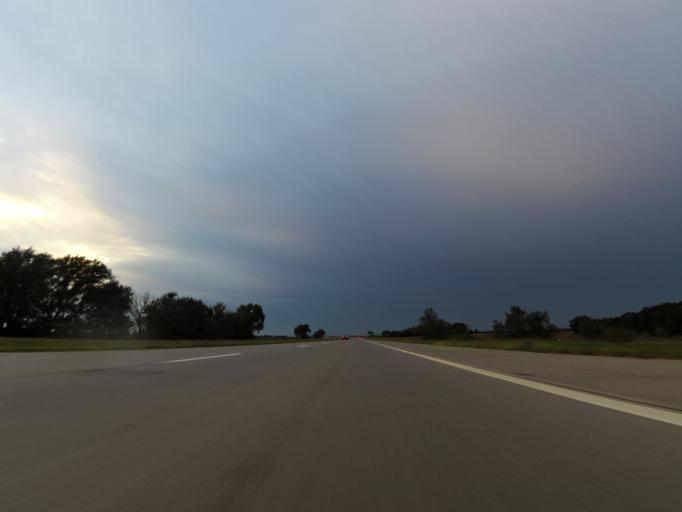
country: US
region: Kansas
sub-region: Sedgwick County
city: Colwich
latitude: 37.8644
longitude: -97.6199
